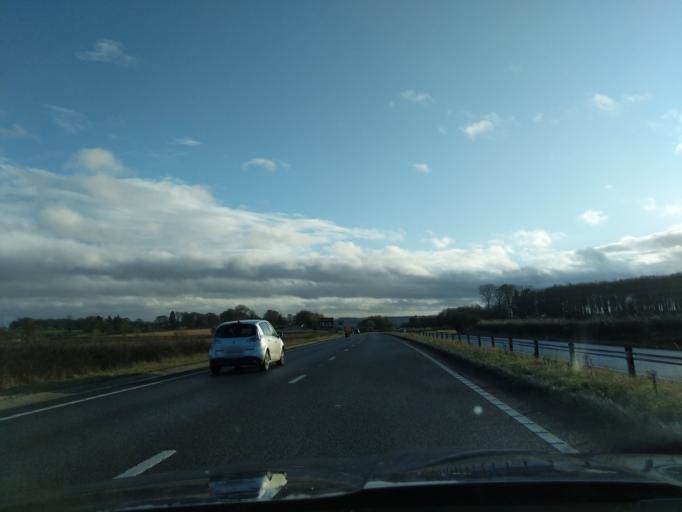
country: GB
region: England
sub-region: Northumberland
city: Alnwick
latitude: 55.4266
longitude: -1.6871
